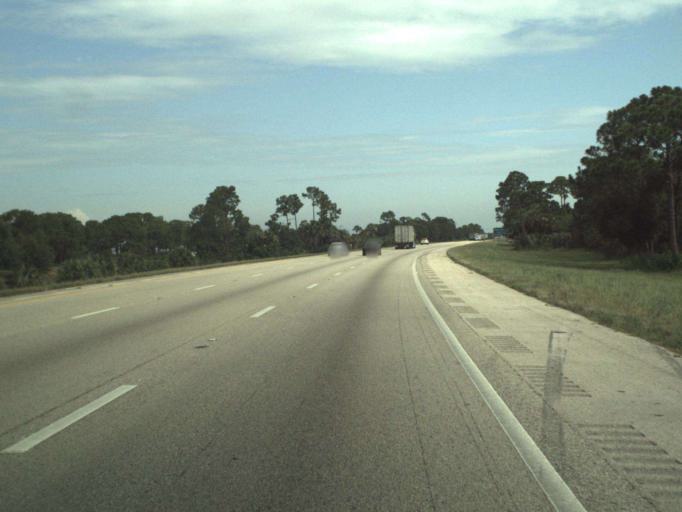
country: US
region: Florida
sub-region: Saint Lucie County
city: Port Saint Lucie
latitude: 27.2380
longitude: -80.4103
